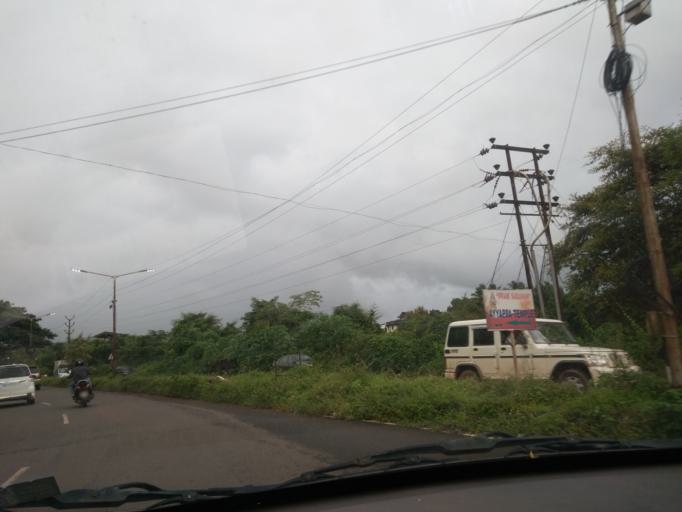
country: IN
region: Goa
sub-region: South Goa
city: Davorlim
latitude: 15.2820
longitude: 73.9801
